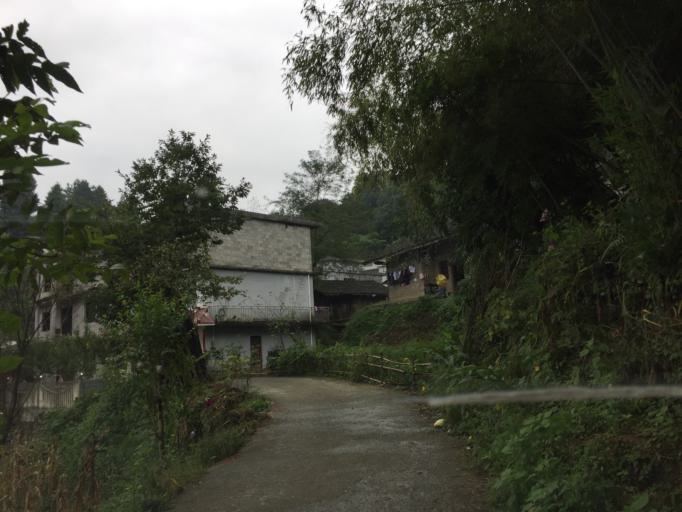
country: CN
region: Guizhou Sheng
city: Longquan
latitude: 28.2115
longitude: 108.0559
